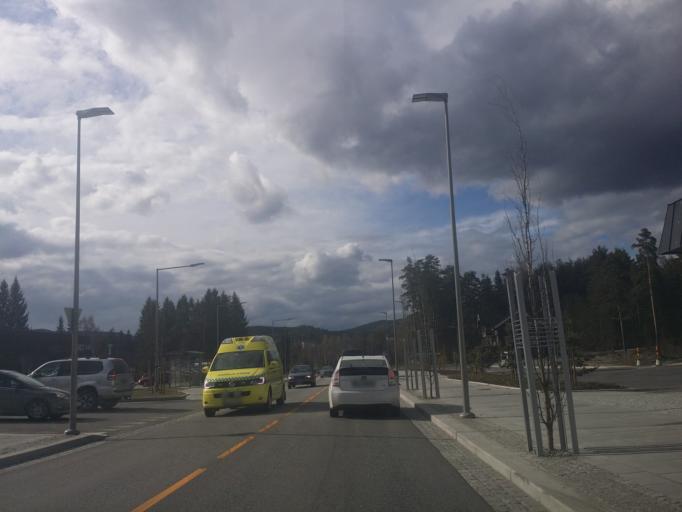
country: NO
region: Buskerud
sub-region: Modum
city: Vikersund
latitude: 60.2396
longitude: 9.9265
